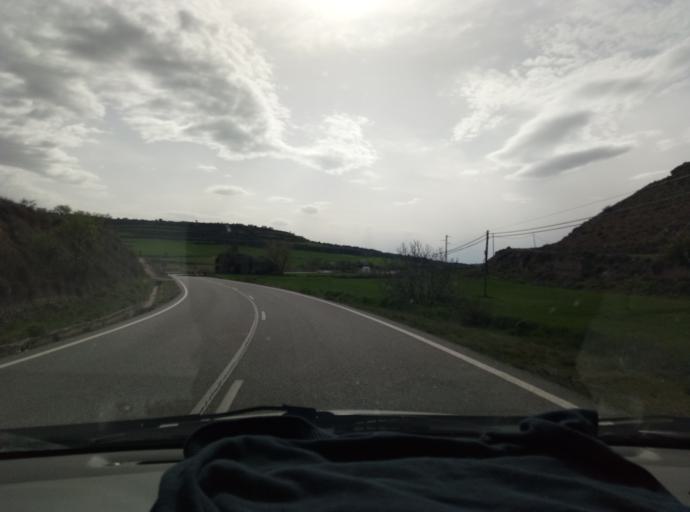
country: ES
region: Catalonia
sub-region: Provincia de Lleida
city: Cervera
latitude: 41.6647
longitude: 1.2638
